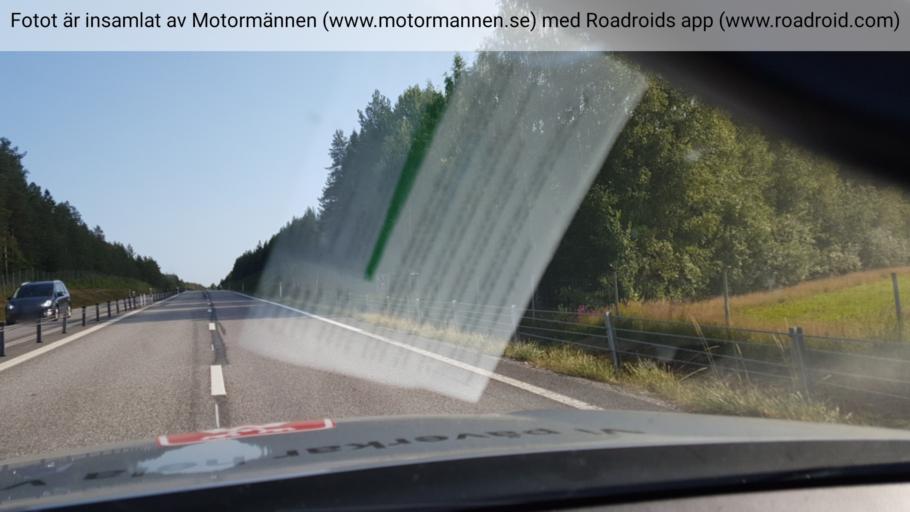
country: SE
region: Norrbotten
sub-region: Pitea Kommun
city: Pitea
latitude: 65.2522
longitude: 21.4766
